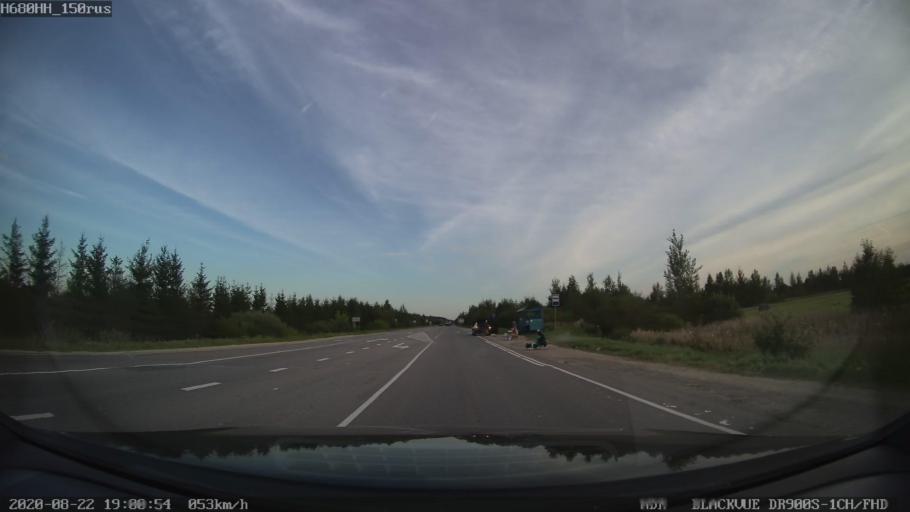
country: RU
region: Tverskaya
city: Vasil'yevskiy Mokh
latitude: 57.1246
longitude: 36.1123
